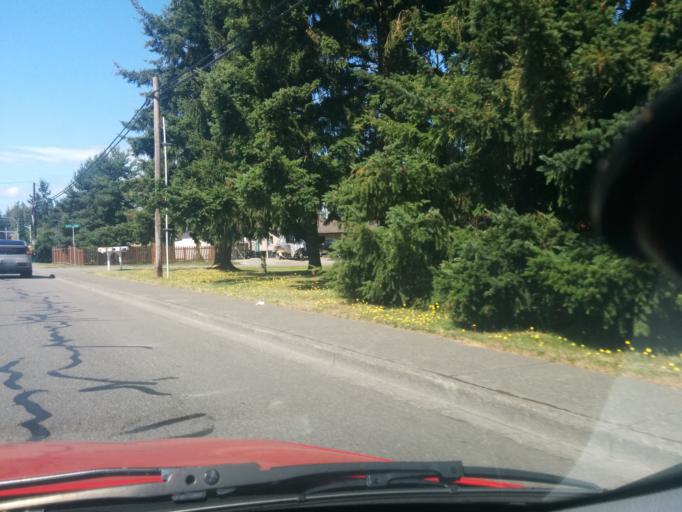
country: US
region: Washington
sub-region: Skagit County
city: Mount Vernon
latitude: 48.4283
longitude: -122.3114
